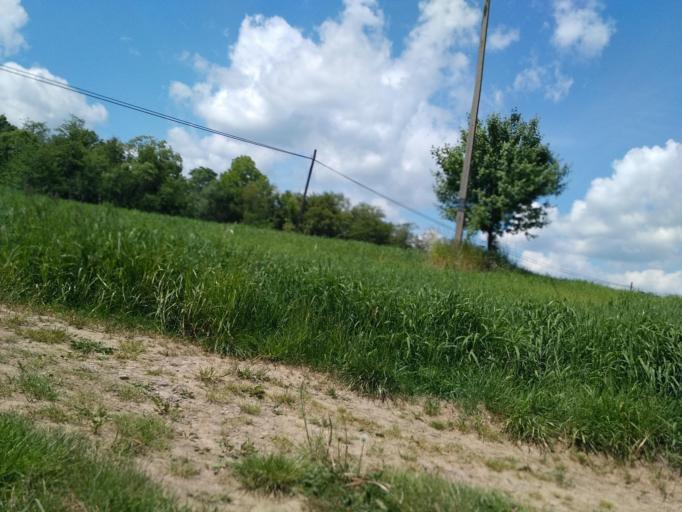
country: PL
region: Subcarpathian Voivodeship
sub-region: Powiat krosnienski
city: Dukla
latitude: 49.5983
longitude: 21.7096
